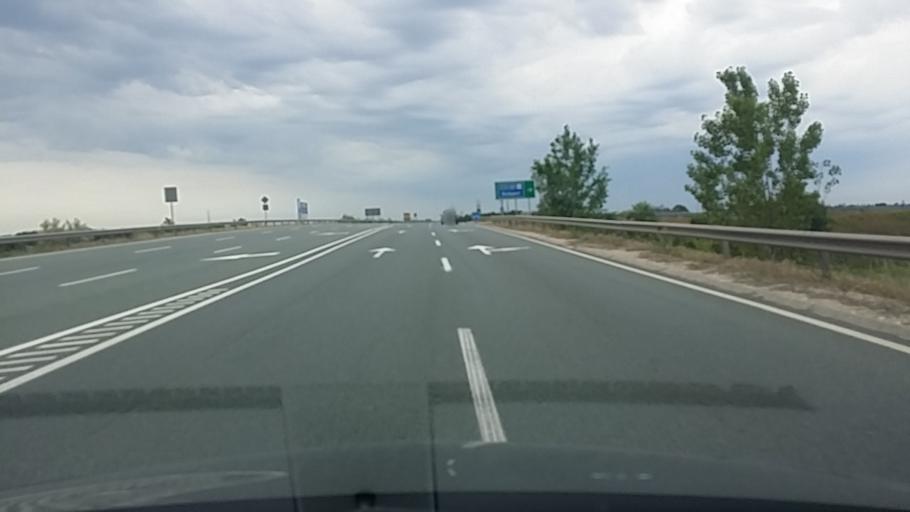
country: HU
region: Fejer
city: dunaujvaros
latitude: 46.9932
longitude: 18.8885
